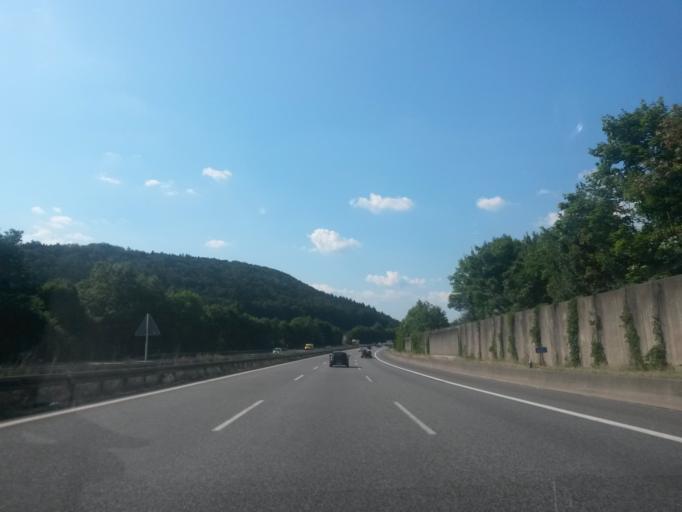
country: DE
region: Bavaria
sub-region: Regierungsbezirk Mittelfranken
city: Greding
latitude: 49.0299
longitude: 11.3636
